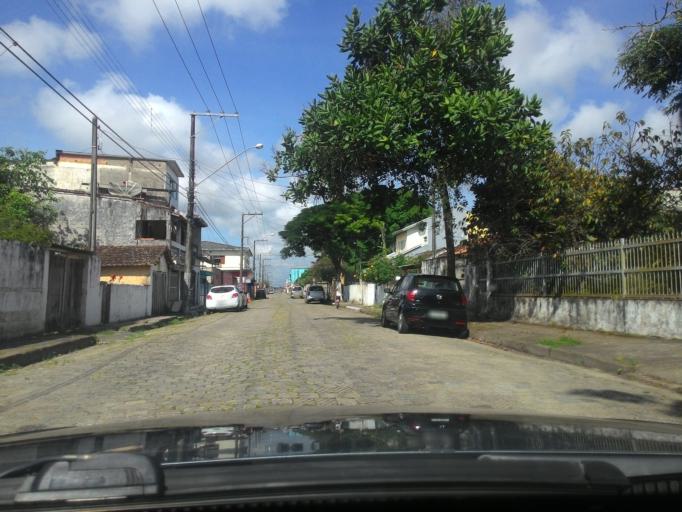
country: BR
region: Sao Paulo
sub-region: Iguape
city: Iguape
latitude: -24.7078
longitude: -47.5588
